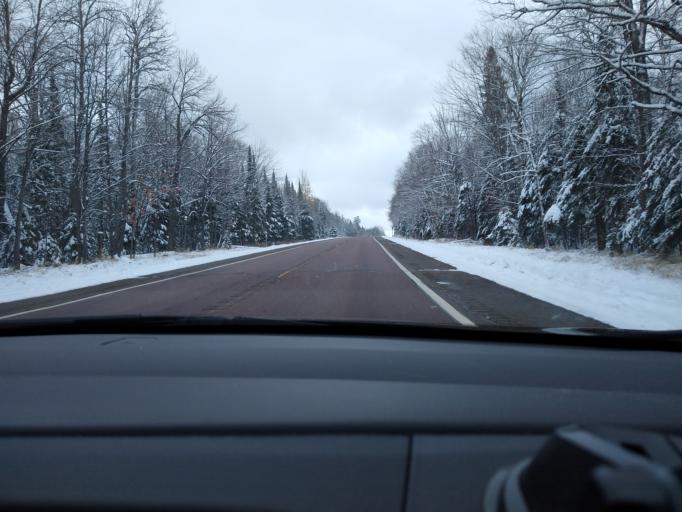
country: US
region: Michigan
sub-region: Iron County
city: Iron River
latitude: 46.1806
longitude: -88.9613
